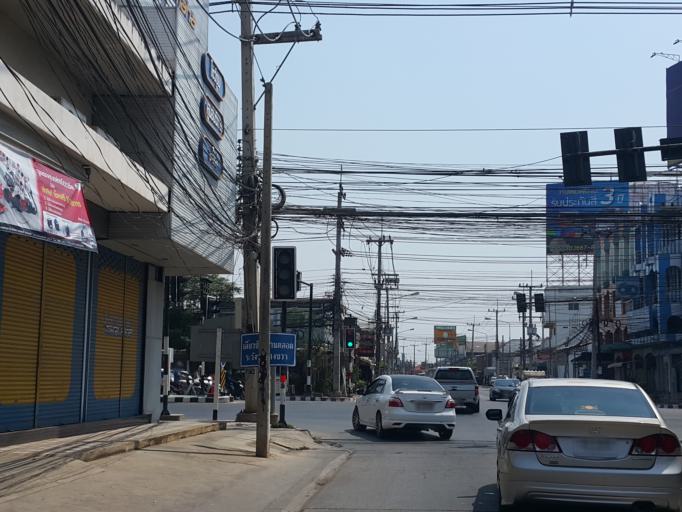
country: TH
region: Phitsanulok
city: Phitsanulok
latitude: 16.8315
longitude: 100.2490
